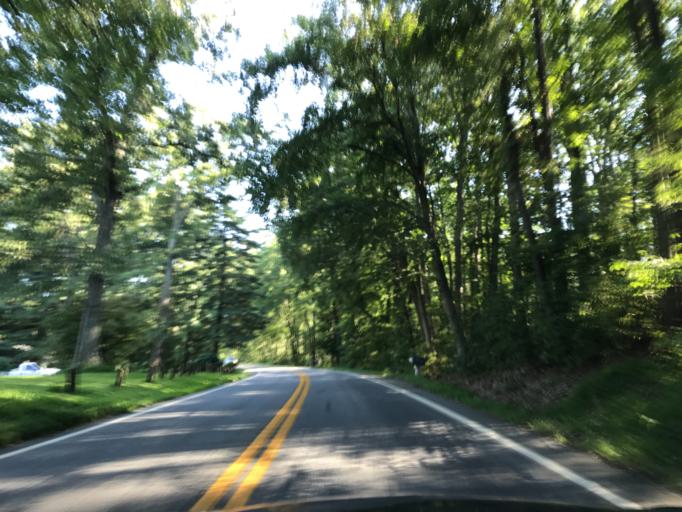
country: US
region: Maryland
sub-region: Harford County
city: Jarrettsville
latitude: 39.6038
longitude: -76.5784
